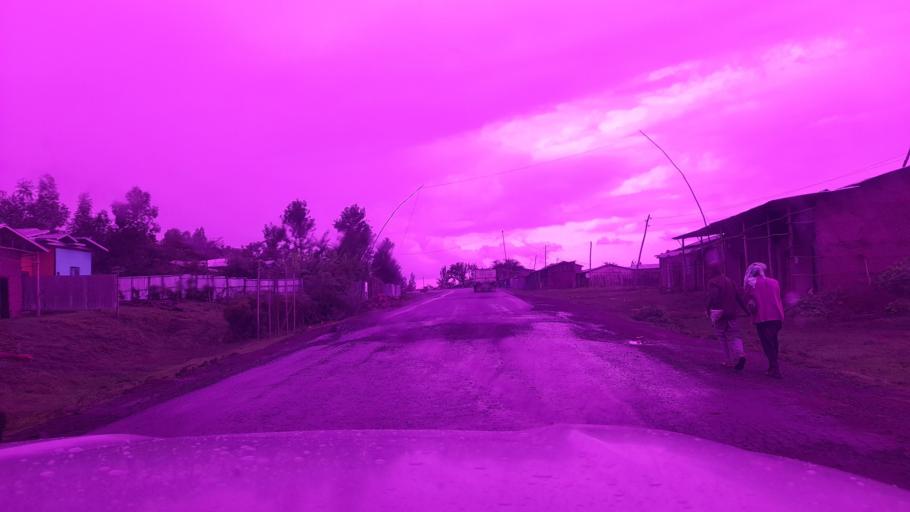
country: ET
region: Oromiya
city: Jima
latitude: 7.7147
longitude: 37.0970
